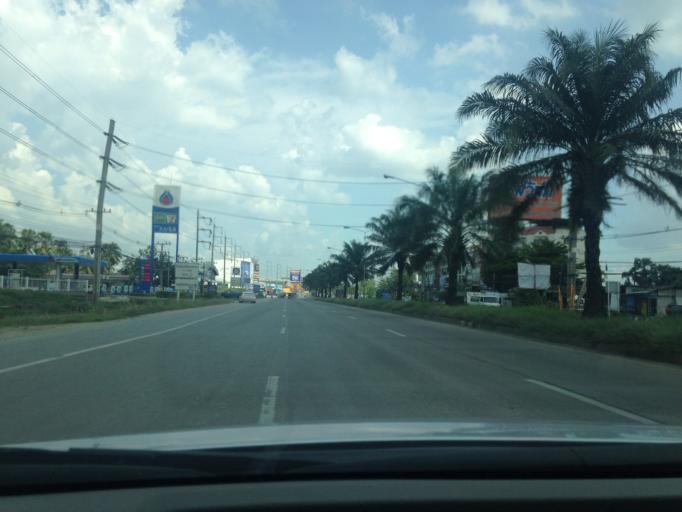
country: TH
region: Pathum Thani
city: Pathum Thani
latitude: 14.0300
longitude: 100.5300
